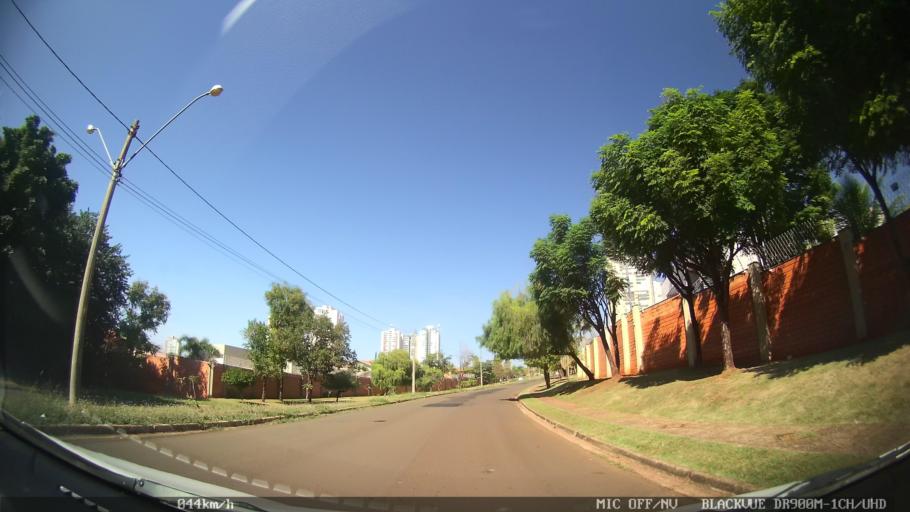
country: BR
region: Sao Paulo
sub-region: Ribeirao Preto
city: Ribeirao Preto
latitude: -21.2129
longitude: -47.8015
